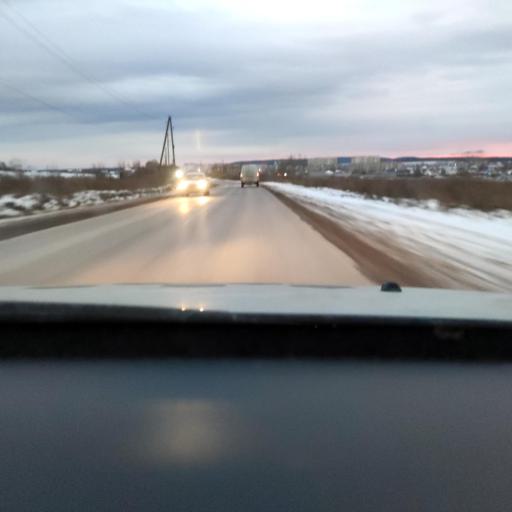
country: RU
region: Perm
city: Gamovo
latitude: 57.8808
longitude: 56.1020
